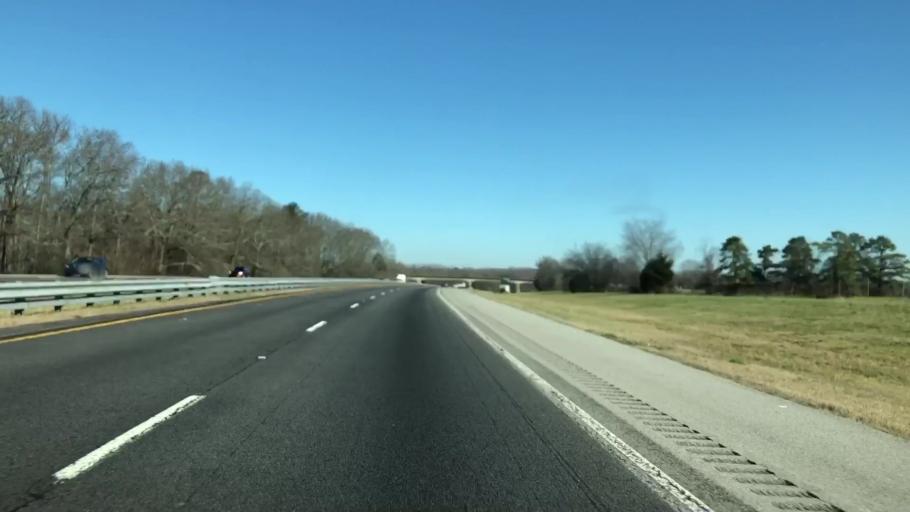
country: US
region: Alabama
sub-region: Limestone County
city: Athens
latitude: 34.8879
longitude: -86.9167
